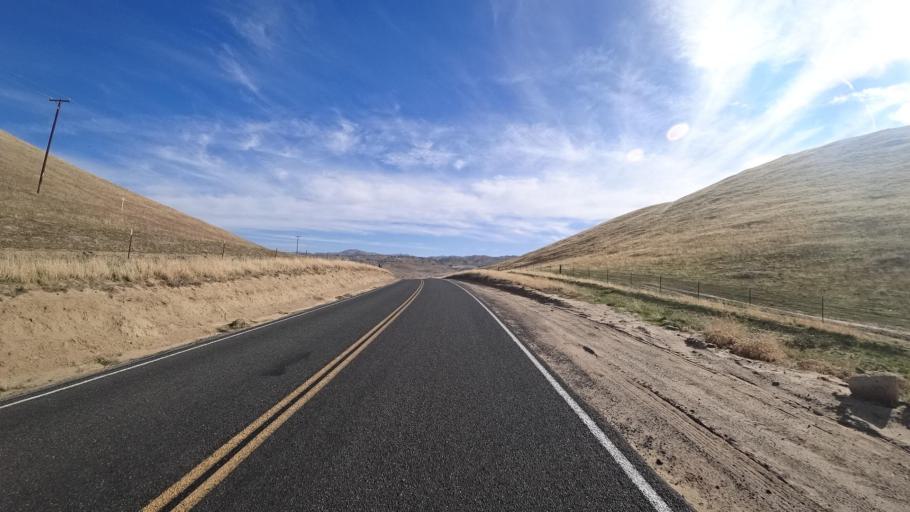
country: US
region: California
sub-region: Kern County
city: Oildale
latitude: 35.6107
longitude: -118.8878
